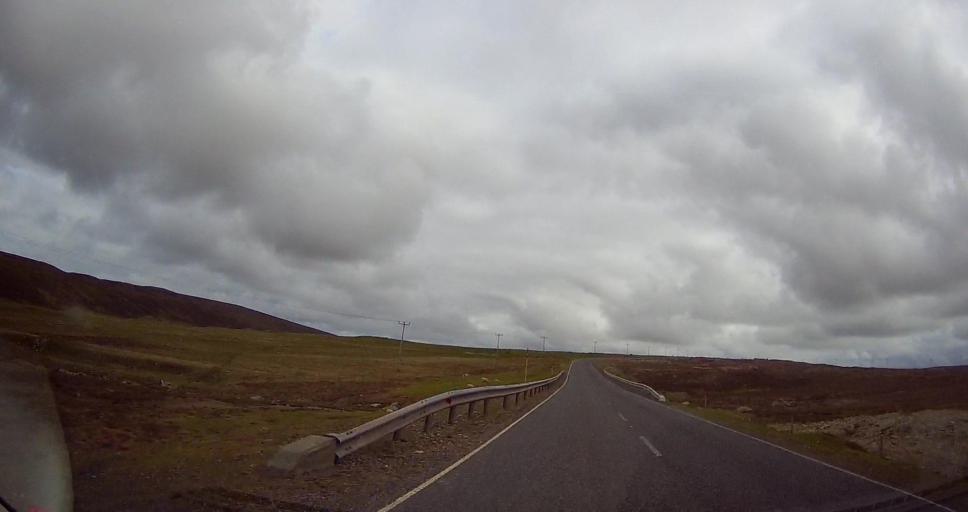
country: GB
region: Scotland
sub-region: Shetland Islands
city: Shetland
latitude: 60.7207
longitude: -0.9104
